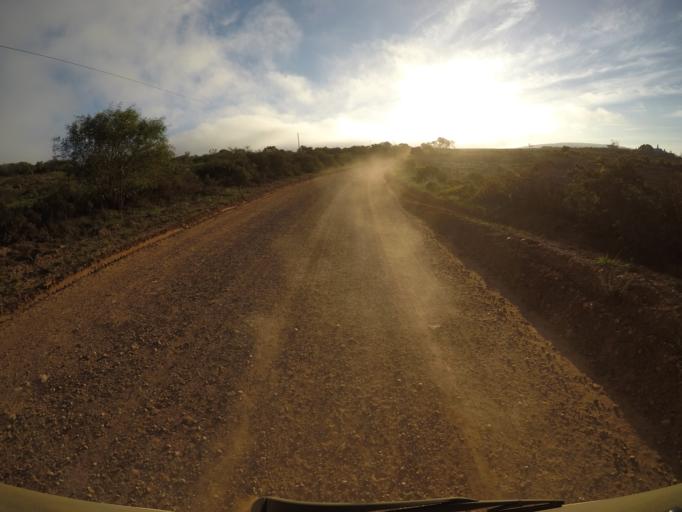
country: ZA
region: Western Cape
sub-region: Eden District Municipality
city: Mossel Bay
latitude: -34.1448
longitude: 22.0187
